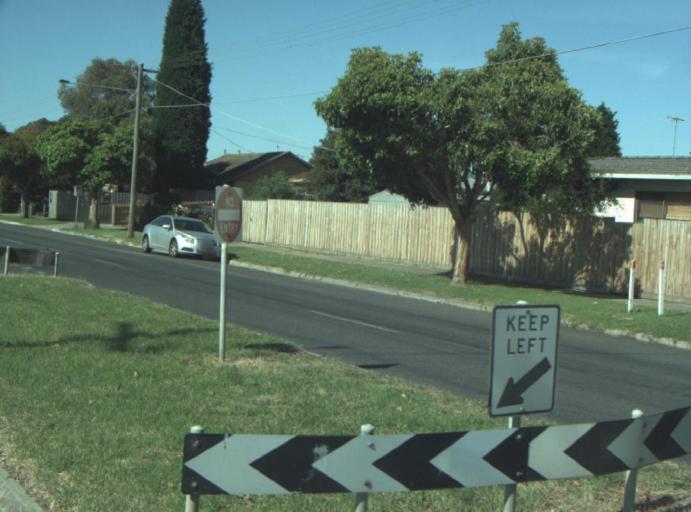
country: AU
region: Victoria
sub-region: Greater Geelong
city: Bell Park
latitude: -38.0888
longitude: 144.3668
